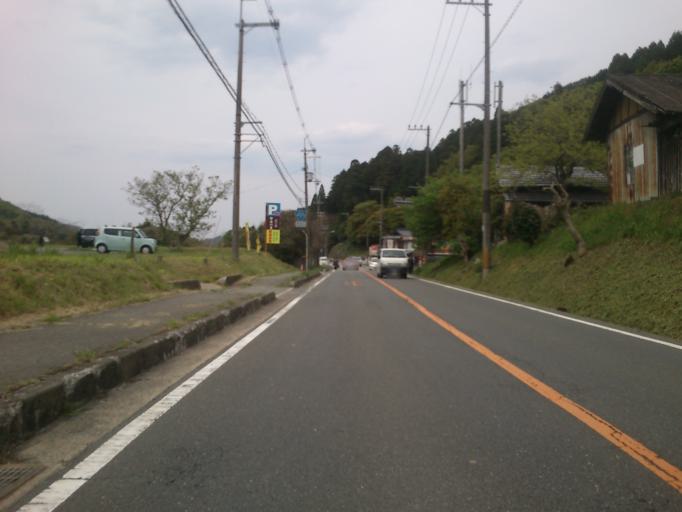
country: JP
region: Kyoto
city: Kameoka
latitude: 34.9425
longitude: 135.4965
